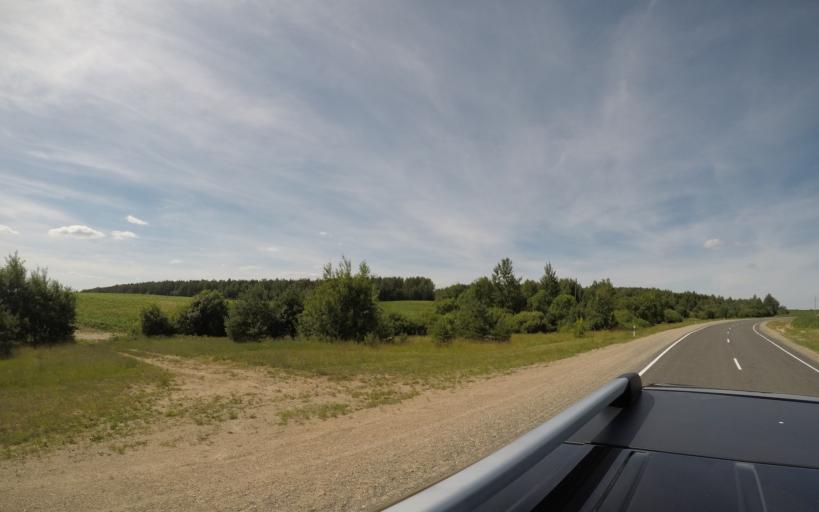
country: BY
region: Grodnenskaya
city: Hal'shany
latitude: 54.2639
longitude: 25.9875
